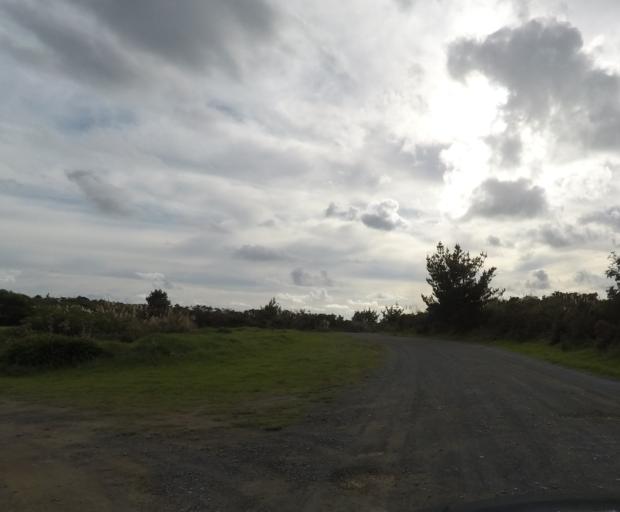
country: NZ
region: Northland
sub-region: Whangarei
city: Ruakaka
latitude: -35.9325
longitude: 174.4590
